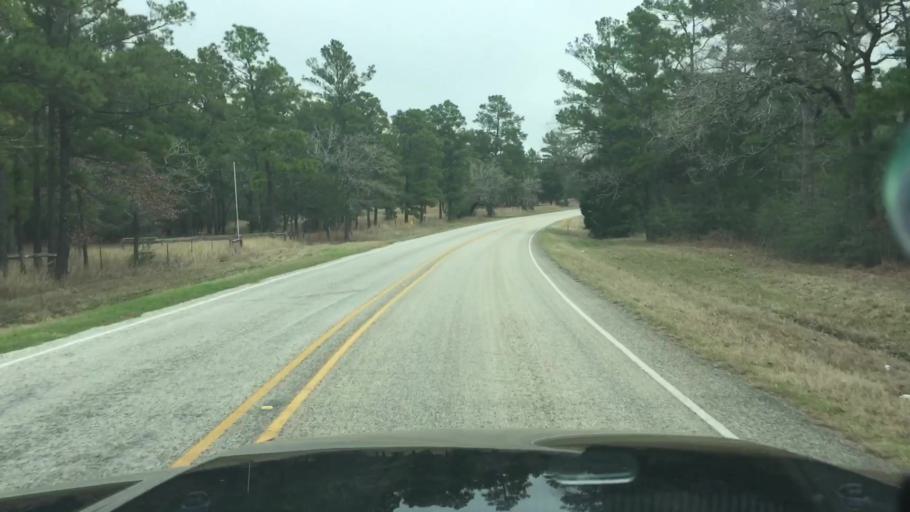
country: US
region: Texas
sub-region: Fayette County
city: La Grange
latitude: 30.0095
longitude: -96.9419
